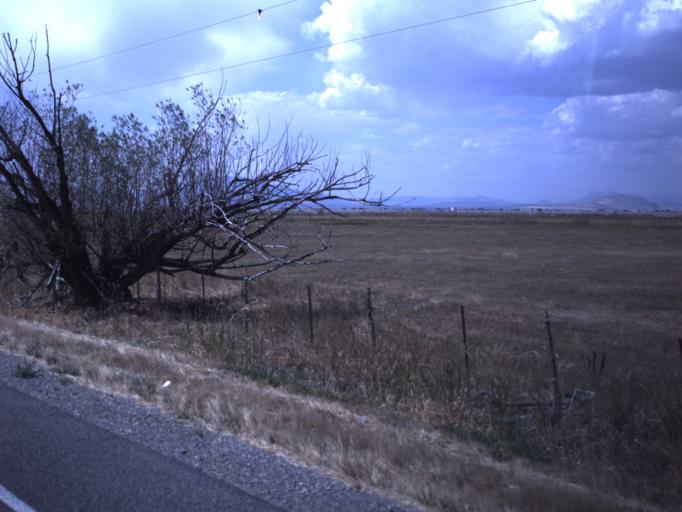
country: US
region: Utah
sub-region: Cache County
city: Logan
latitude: 41.7368
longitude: -111.8917
